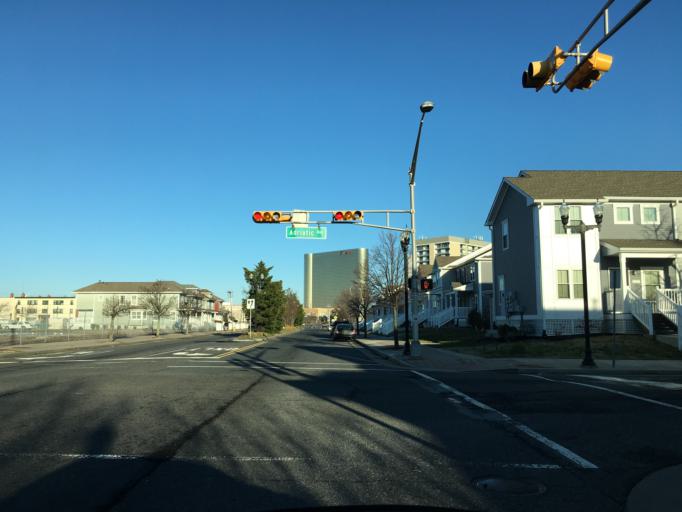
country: US
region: New Jersey
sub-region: Atlantic County
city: Atlantic City
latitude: 39.3685
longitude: -74.4292
